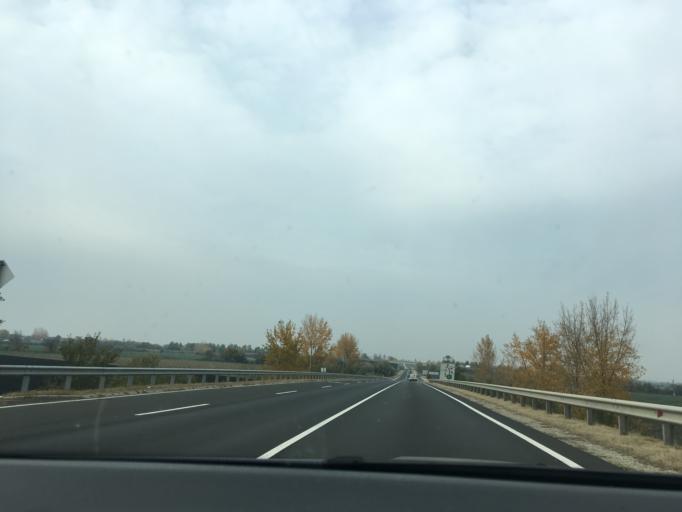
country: HU
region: Jasz-Nagykun-Szolnok
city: Toszeg
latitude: 47.1772
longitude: 20.1013
